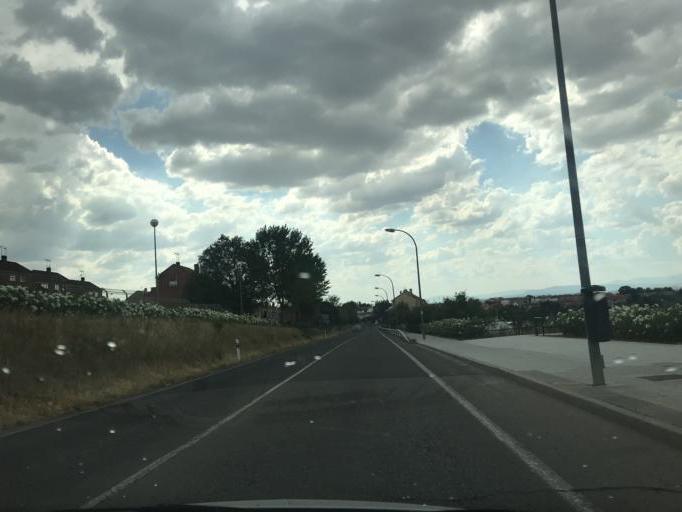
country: ES
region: Madrid
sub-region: Provincia de Madrid
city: Paracuellos de Jarama
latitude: 40.5055
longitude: -3.5238
